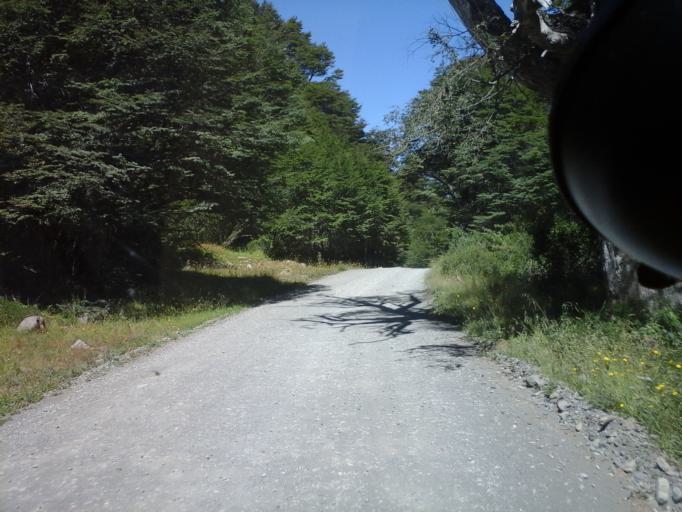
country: AR
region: Neuquen
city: Villa La Angostura
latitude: -41.2148
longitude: -71.8012
